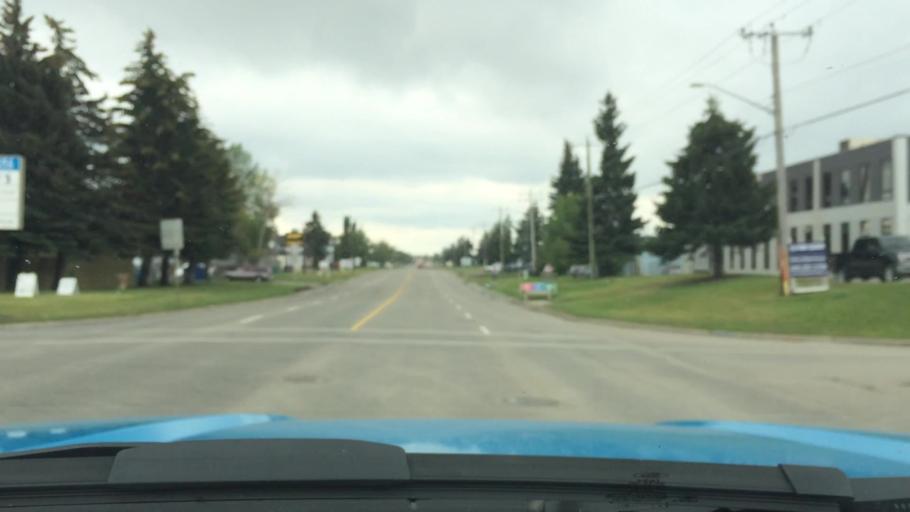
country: CA
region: Alberta
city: Calgary
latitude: 51.0884
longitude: -114.0117
